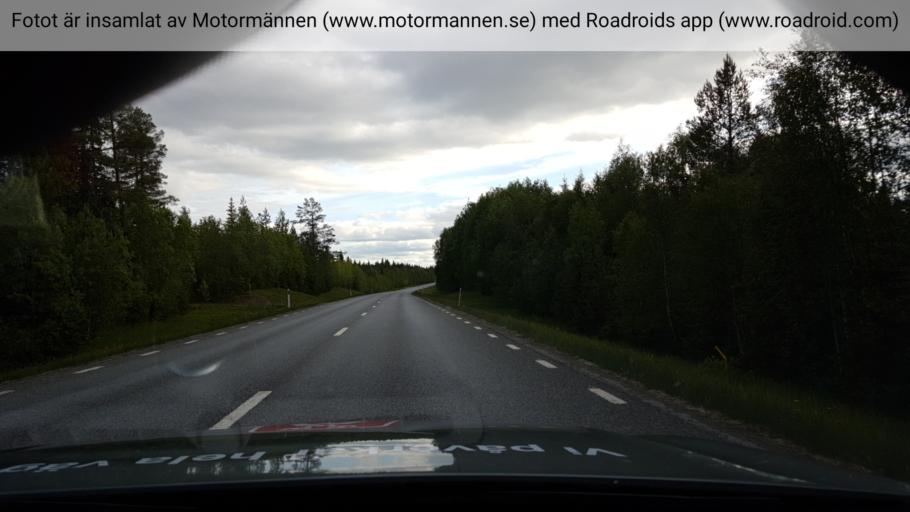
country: SE
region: Jaemtland
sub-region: OEstersunds Kommun
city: Lit
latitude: 63.4318
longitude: 15.1212
